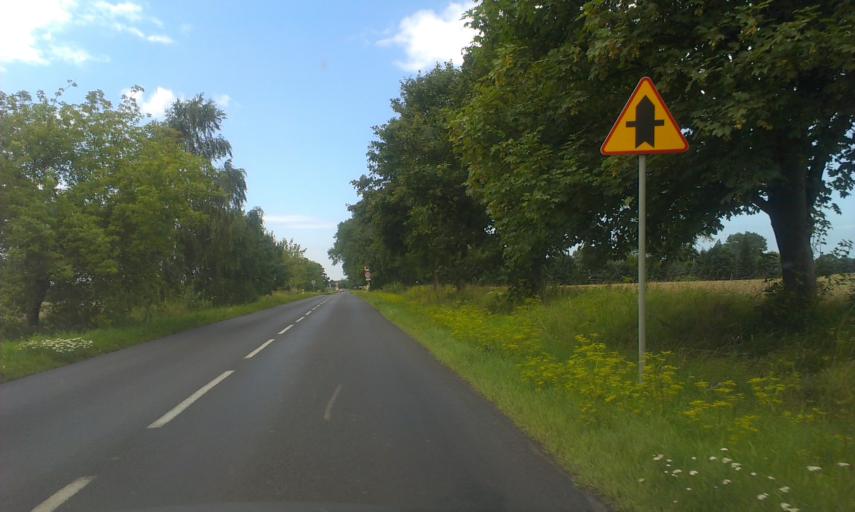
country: PL
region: West Pomeranian Voivodeship
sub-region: Powiat kolobrzeski
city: Dygowo
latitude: 54.1453
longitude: 15.6815
